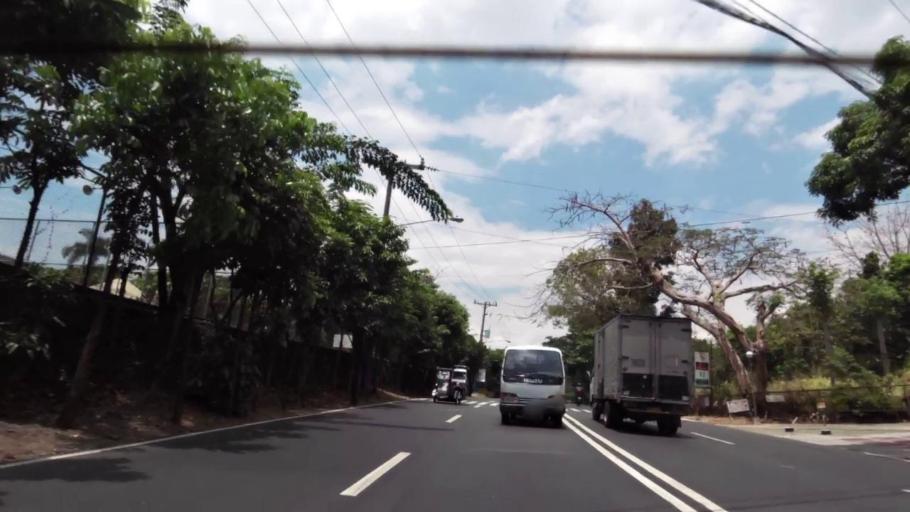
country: PH
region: Calabarzon
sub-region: Province of Rizal
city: Antipolo
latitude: 14.6113
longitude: 121.1582
